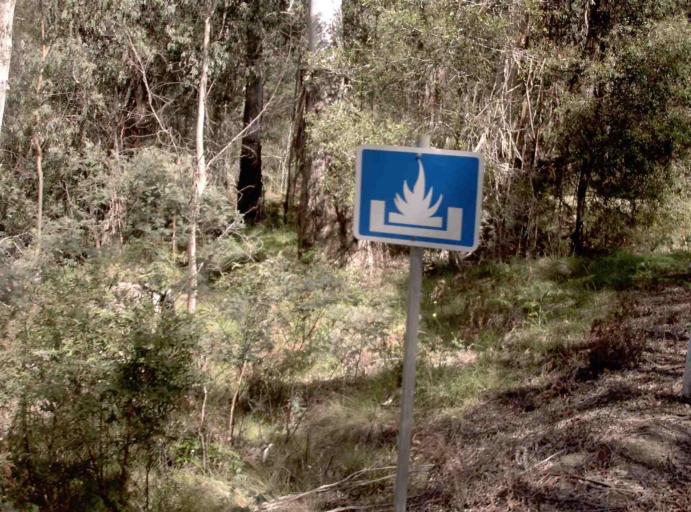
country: AU
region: New South Wales
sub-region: Bombala
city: Bombala
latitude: -37.1529
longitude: 148.7246
